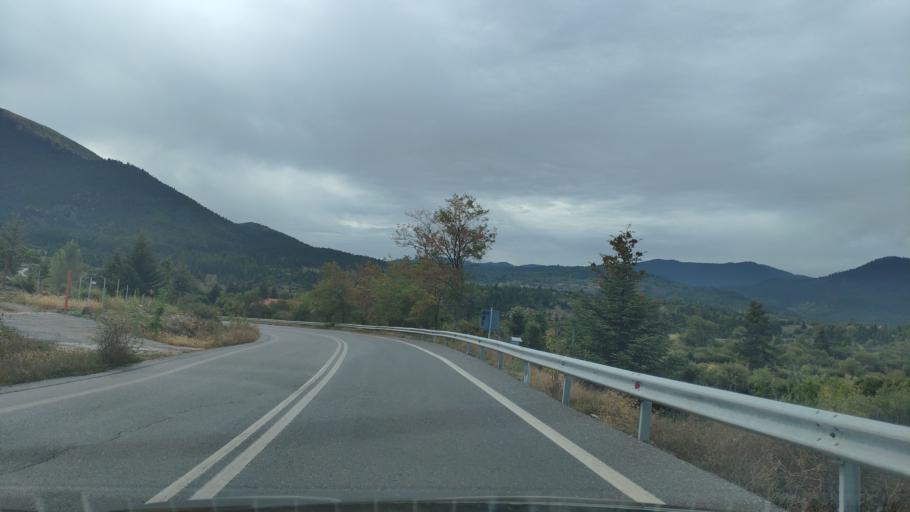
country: GR
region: Peloponnese
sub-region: Nomos Arkadias
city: Dimitsana
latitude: 37.6575
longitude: 22.1878
